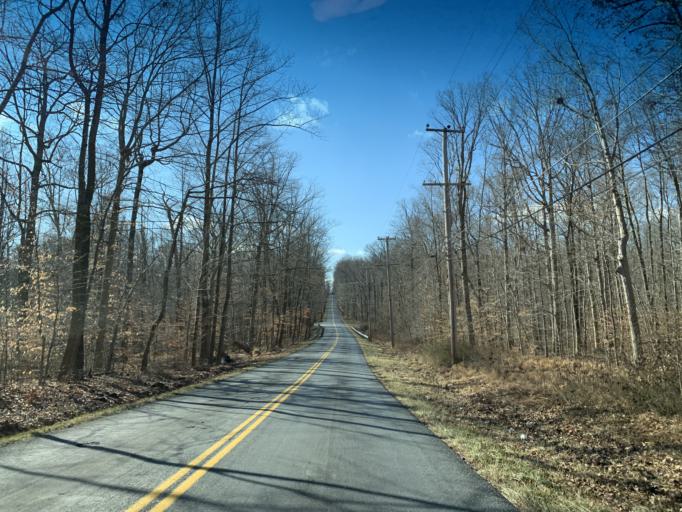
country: US
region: Maryland
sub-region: Harford County
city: Riverside
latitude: 39.5268
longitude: -76.2230
